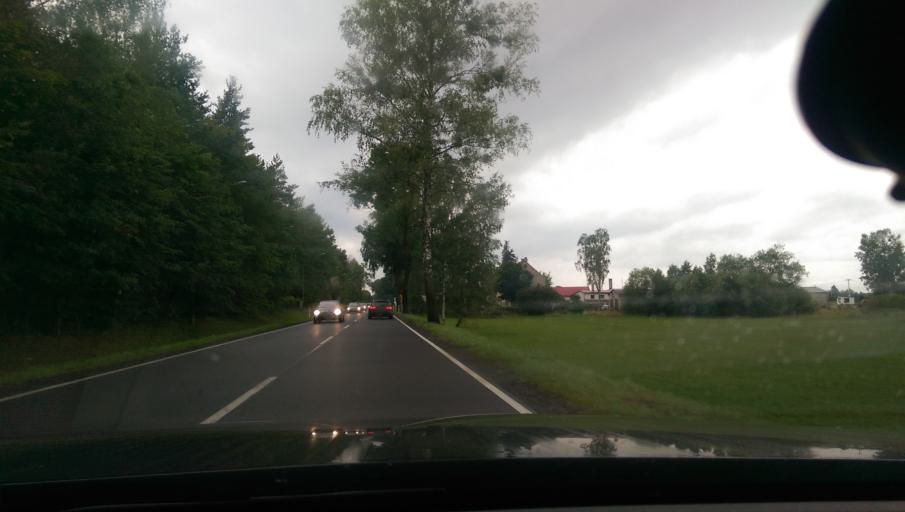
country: PL
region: Warmian-Masurian Voivodeship
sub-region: Powiat szczycienski
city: Szczytno
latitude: 53.5613
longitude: 21.0284
